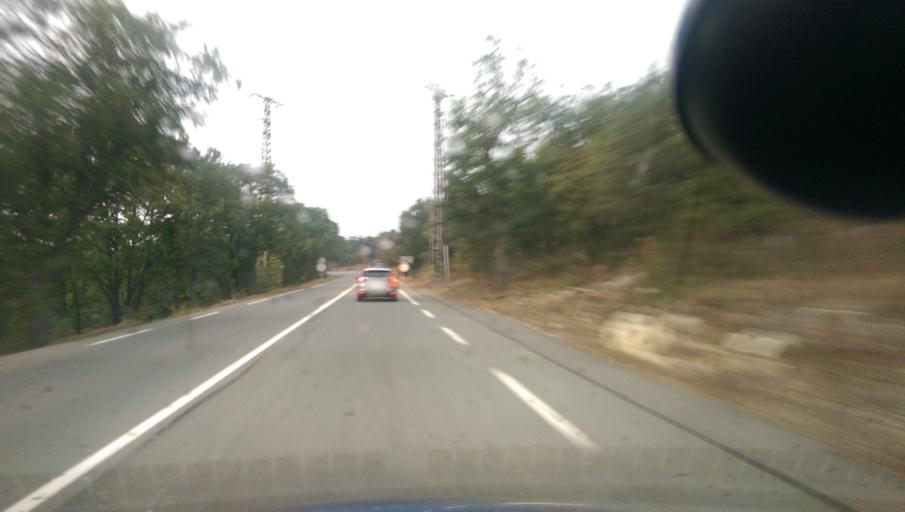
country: FR
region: Provence-Alpes-Cote d'Azur
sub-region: Departement des Alpes-Maritimes
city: Cabris
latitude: 43.6840
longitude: 6.8859
